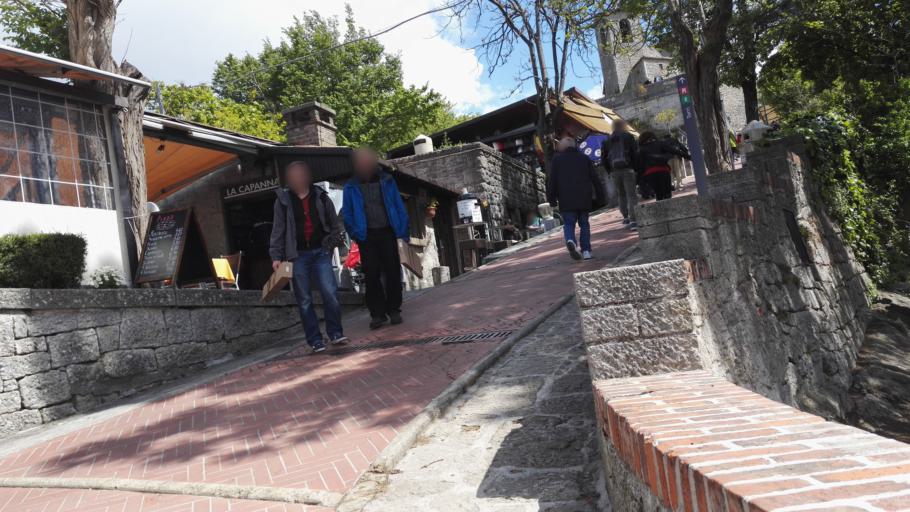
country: SM
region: San Marino
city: San Marino
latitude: 43.9359
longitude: 12.4482
